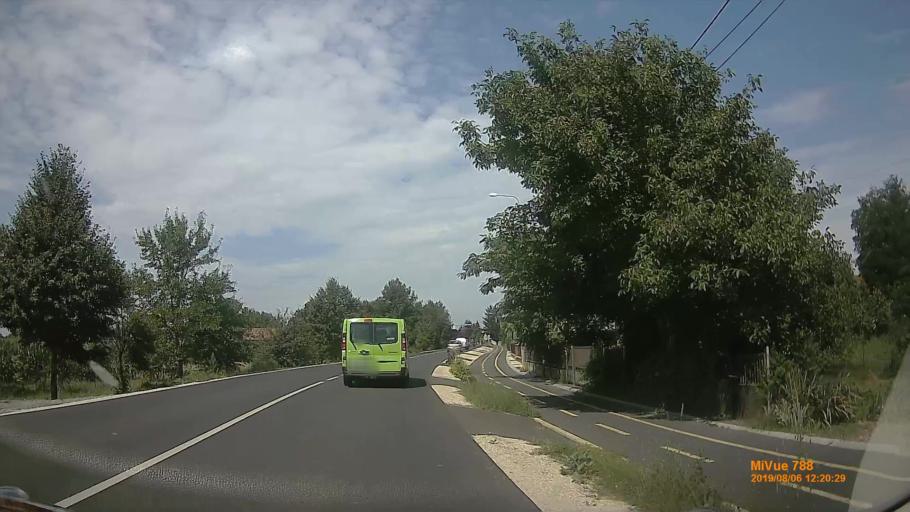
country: HU
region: Vas
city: Taplanszentkereszt
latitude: 47.1804
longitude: 16.7495
